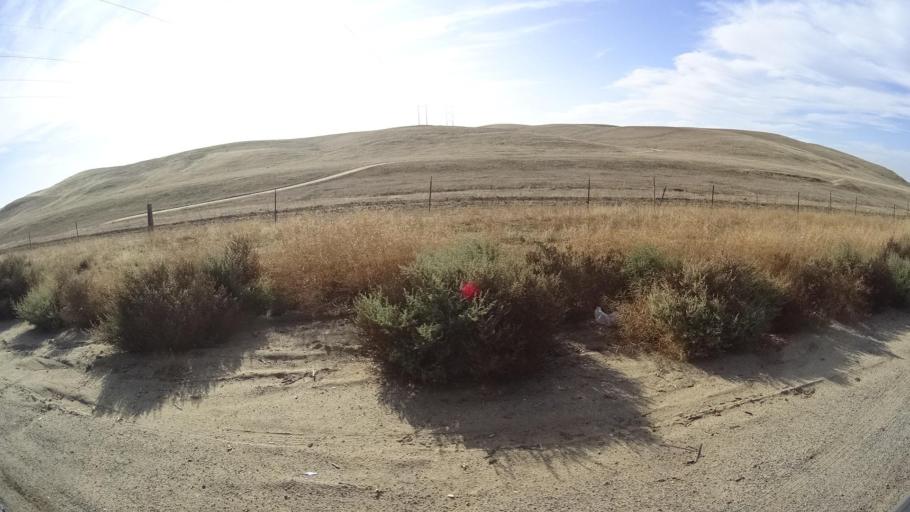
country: US
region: California
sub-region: Tulare County
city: Richgrove
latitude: 35.6200
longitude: -119.0396
